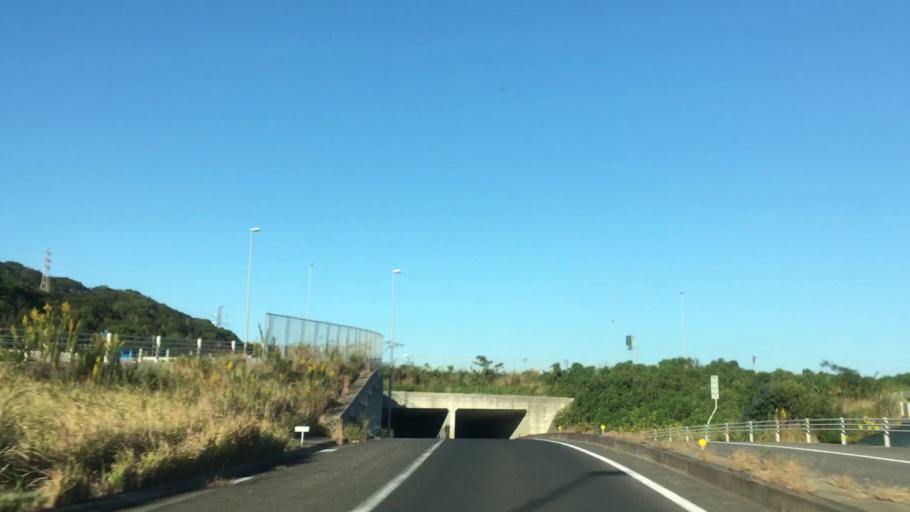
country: JP
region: Nagasaki
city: Sasebo
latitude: 33.2019
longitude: 129.6715
